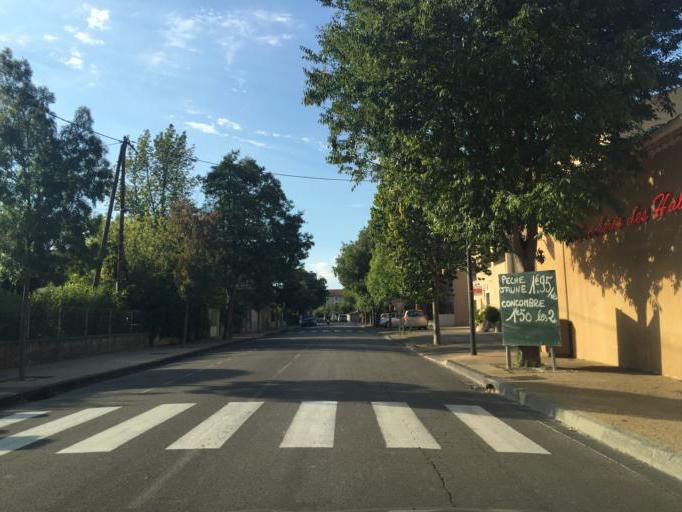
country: FR
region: Provence-Alpes-Cote d'Azur
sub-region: Departement du Vaucluse
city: Pernes-les-Fontaines
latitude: 44.0003
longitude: 5.0615
